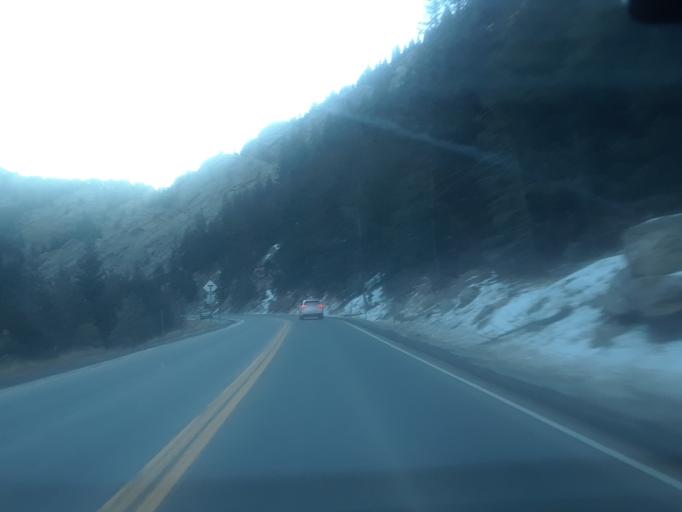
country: US
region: Colorado
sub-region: Clear Creek County
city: Idaho Springs
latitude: 39.7370
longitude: -105.4171
